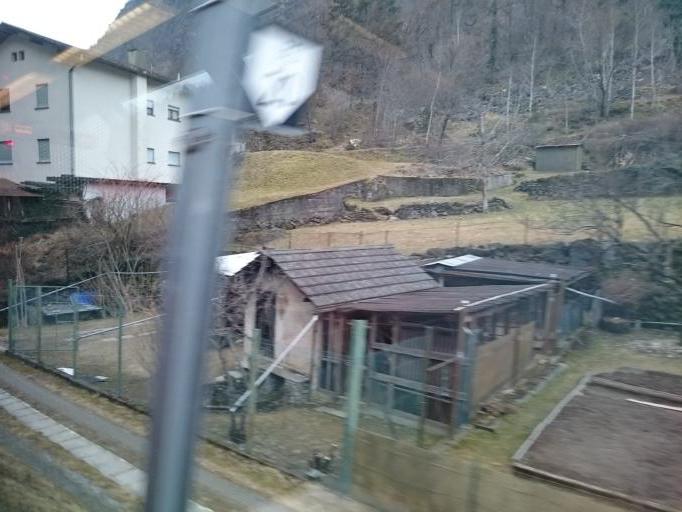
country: IT
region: Lombardy
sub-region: Provincia di Sondrio
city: Tirano
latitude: 46.2306
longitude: 10.1443
